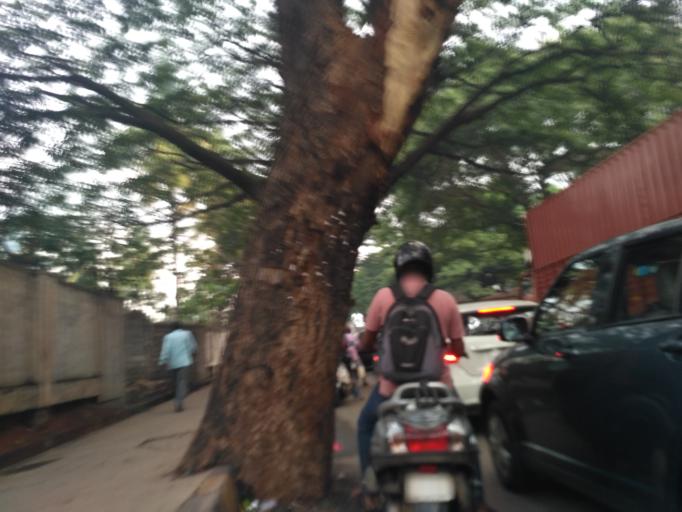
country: IN
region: Karnataka
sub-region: Bangalore Urban
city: Bangalore
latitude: 13.0278
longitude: 77.5356
